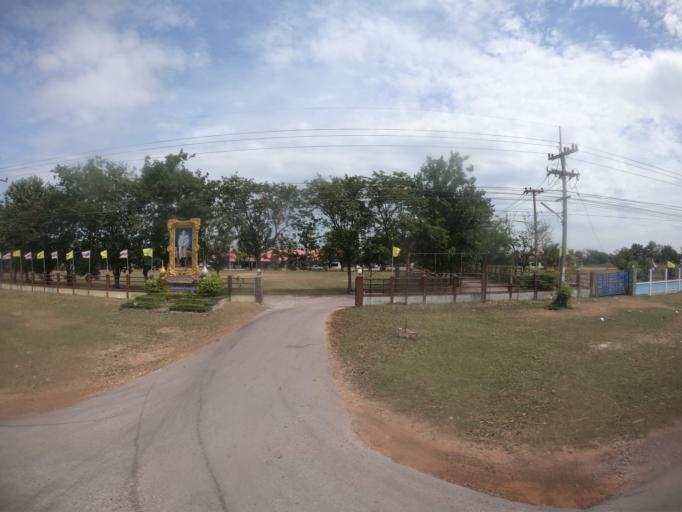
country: TH
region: Maha Sarakham
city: Chiang Yuen
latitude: 16.3629
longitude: 103.1089
